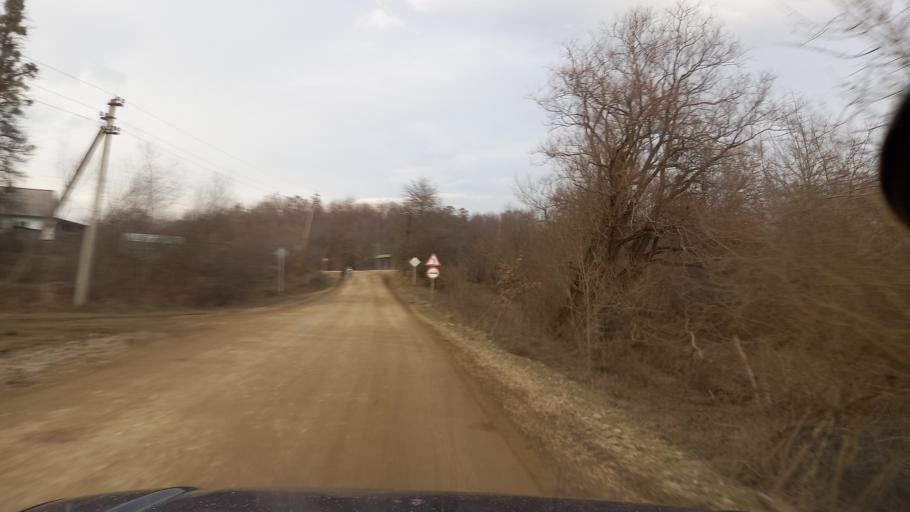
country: RU
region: Adygeya
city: Kamennomostskiy
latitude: 44.1662
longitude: 40.2467
